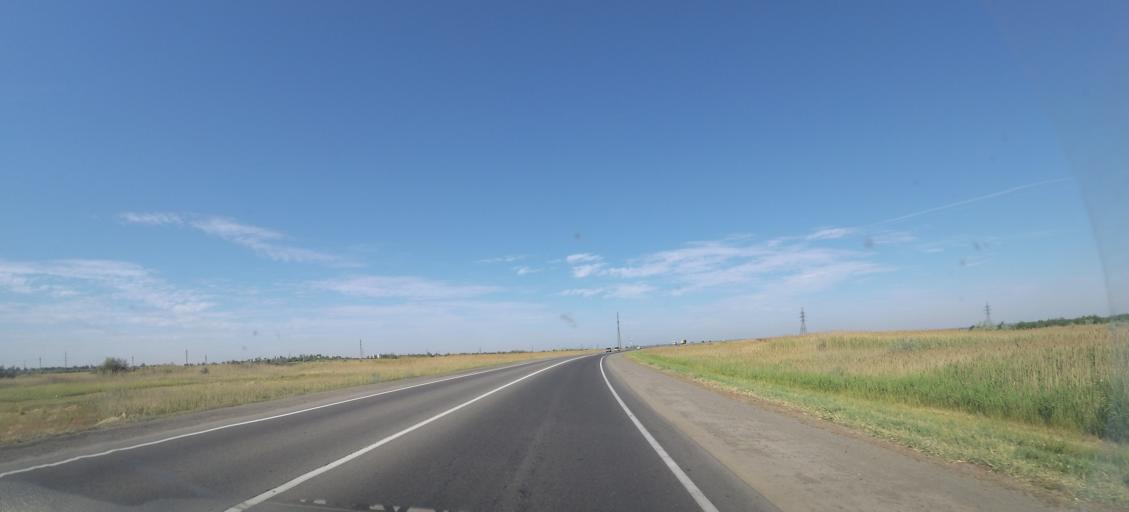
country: RU
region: Volgograd
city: Oktyabr'skiy
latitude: 48.6745
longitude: 43.8844
